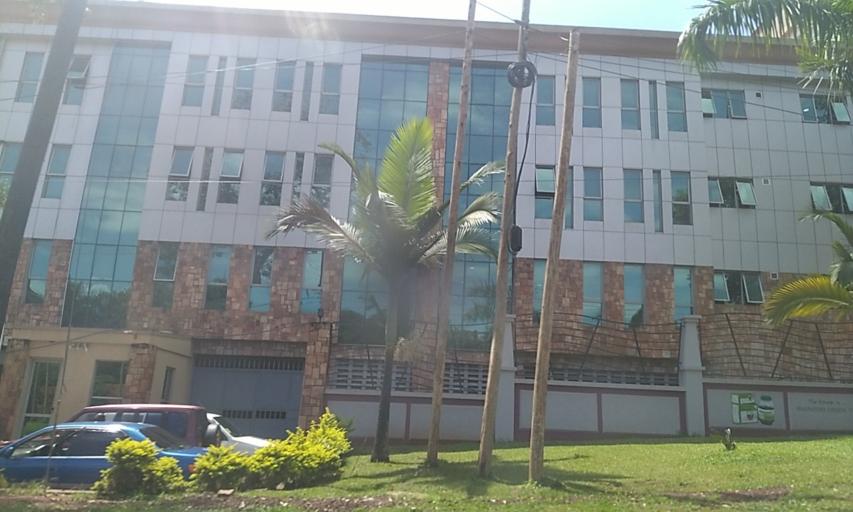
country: UG
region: Central Region
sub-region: Kampala District
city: Kampala
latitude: 0.3270
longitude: 32.5985
